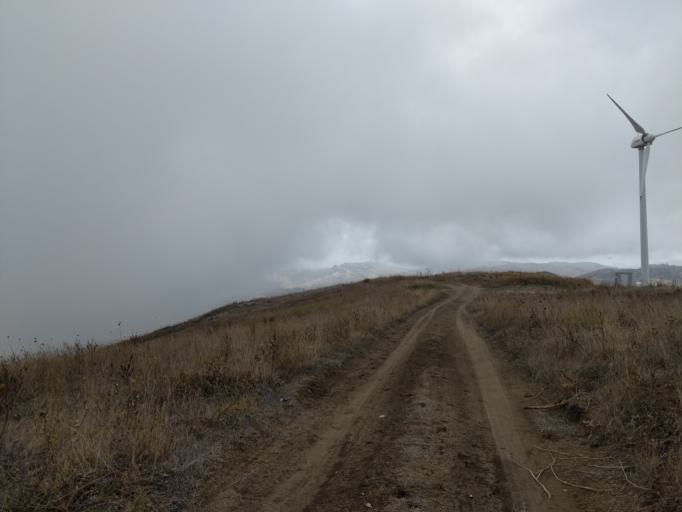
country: IT
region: Sicily
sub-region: Agrigento
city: Comitini
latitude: 37.4079
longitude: 13.6660
